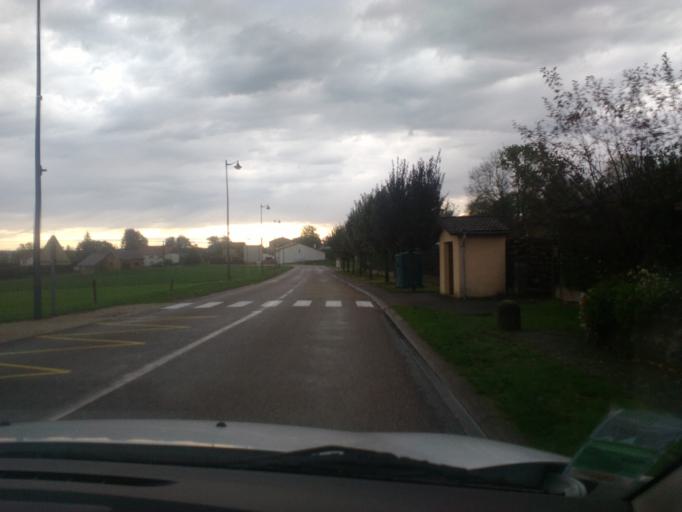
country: FR
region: Lorraine
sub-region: Departement des Vosges
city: Igney
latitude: 48.2934
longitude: 6.4381
